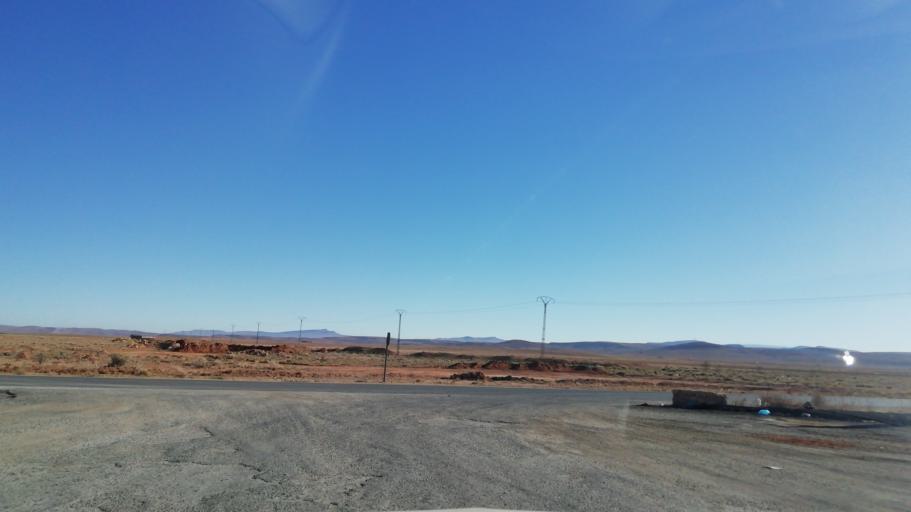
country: DZ
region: El Bayadh
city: El Bayadh
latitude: 33.6553
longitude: 0.9077
